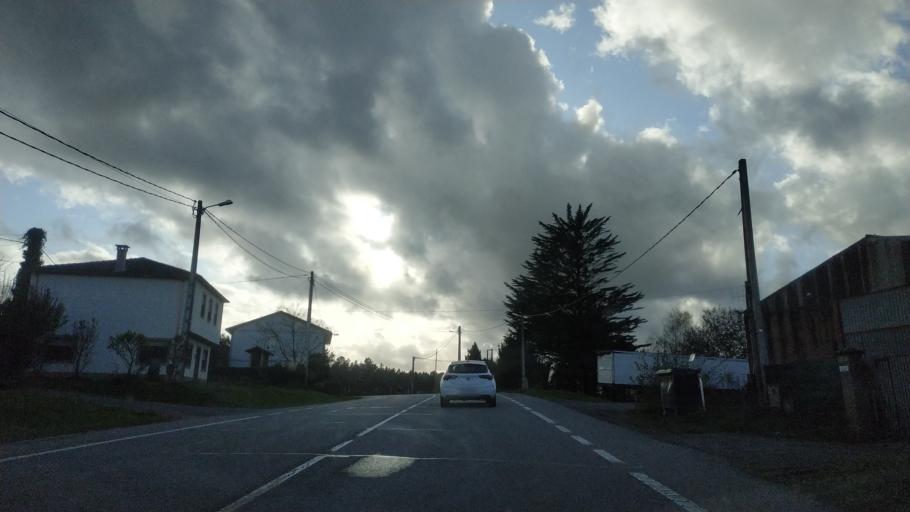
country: ES
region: Galicia
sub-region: Provincia da Coruna
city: Arzua
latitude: 42.9170
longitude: -8.1674
